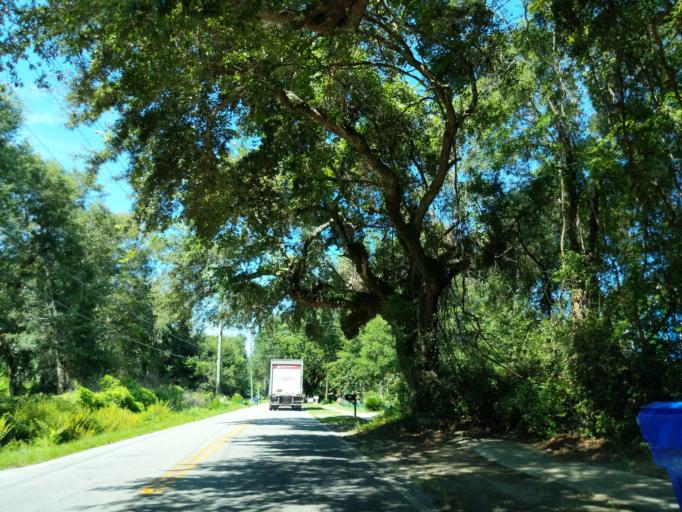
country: US
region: South Carolina
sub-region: Charleston County
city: Charleston
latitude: 32.7241
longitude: -79.9468
